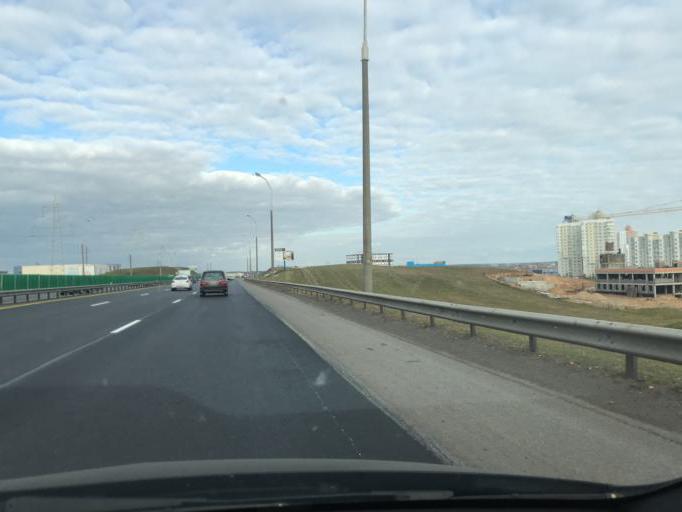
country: BY
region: Minsk
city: Zhdanovichy
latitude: 53.9298
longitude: 27.4209
